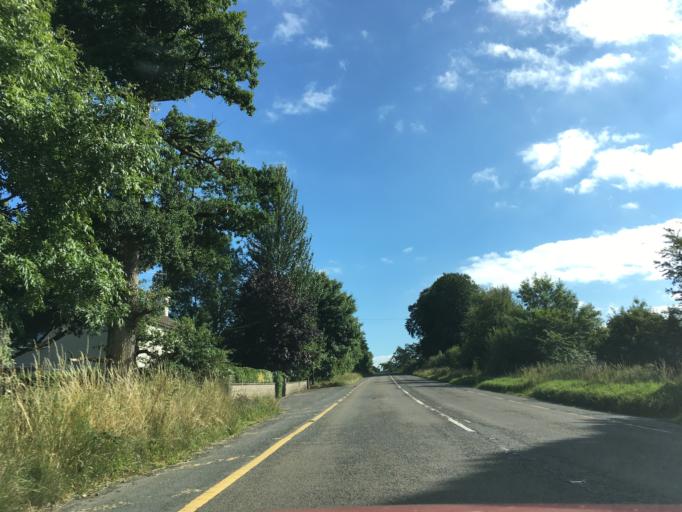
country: IE
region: Munster
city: Cashel
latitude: 52.4842
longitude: -7.8914
